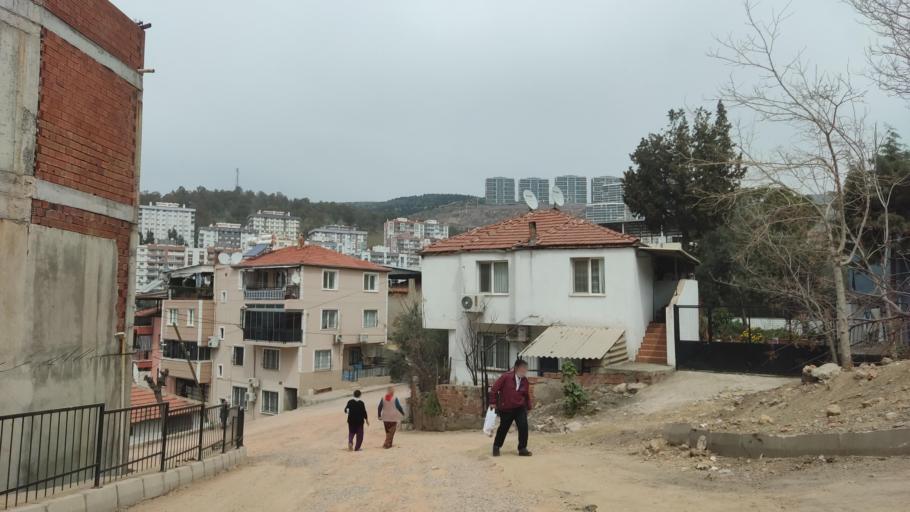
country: TR
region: Izmir
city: Karsiyaka
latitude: 38.5006
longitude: 27.0735
